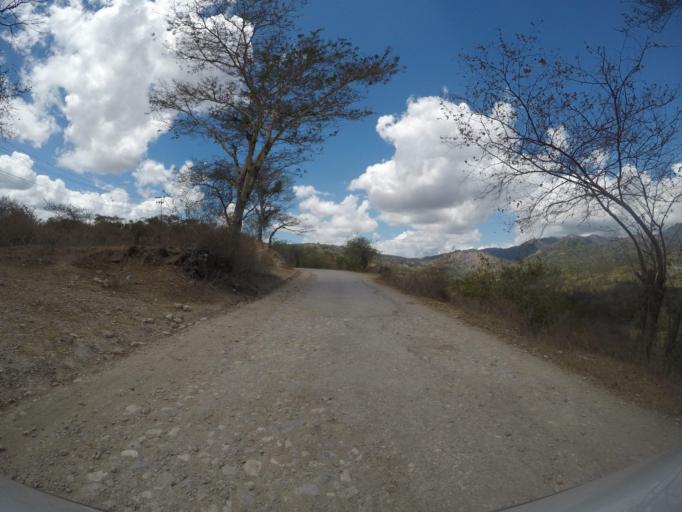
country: TL
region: Baucau
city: Baucau
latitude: -8.4853
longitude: 126.6194
